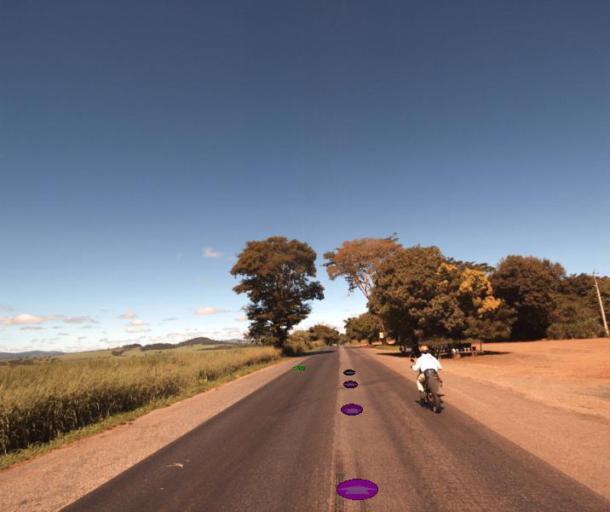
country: BR
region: Goias
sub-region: Itapaci
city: Itapaci
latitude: -15.1205
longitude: -49.5003
